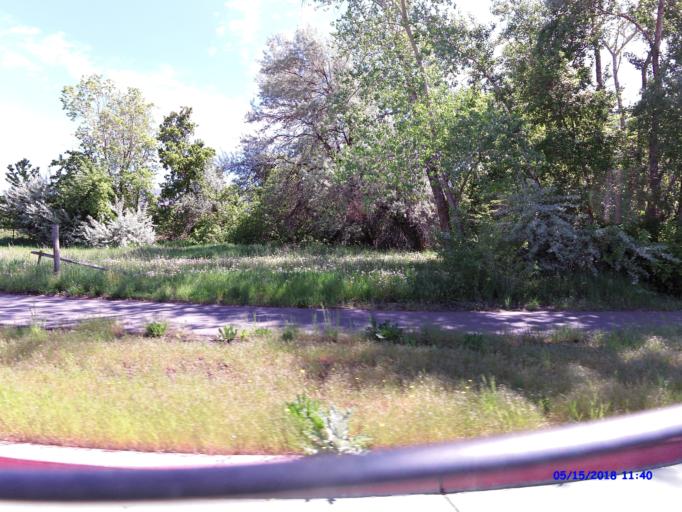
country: US
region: Utah
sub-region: Weber County
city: Washington Terrace
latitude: 41.1745
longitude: -111.9467
